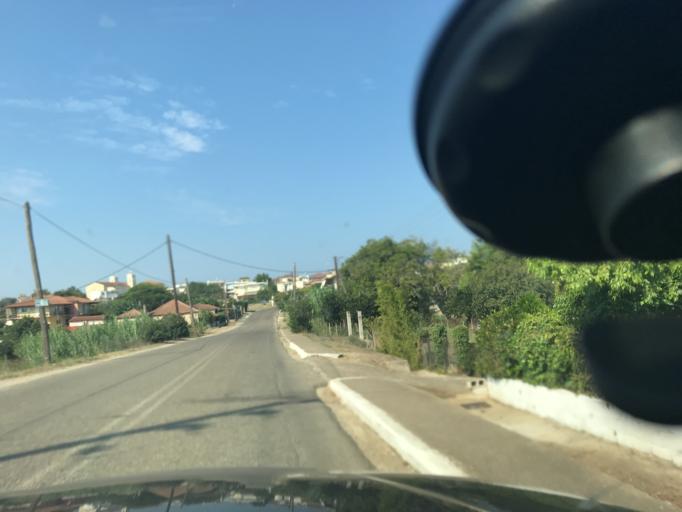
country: GR
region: West Greece
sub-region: Nomos Ileias
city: Kardamas
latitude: 37.7157
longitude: 21.3526
